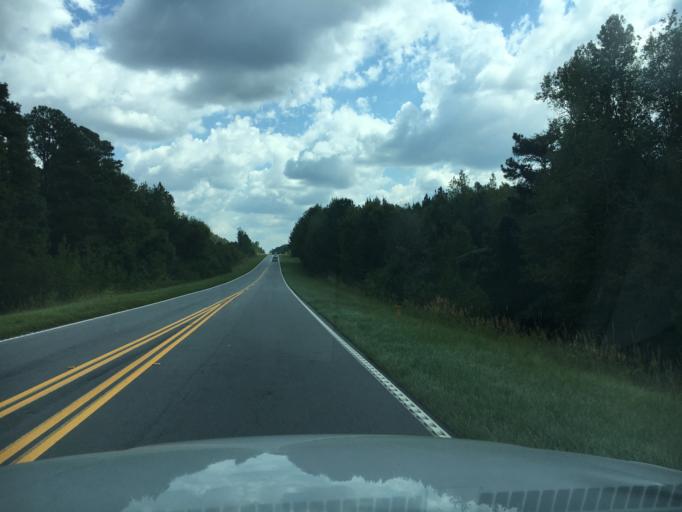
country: US
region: South Carolina
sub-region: Greenwood County
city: Greenwood
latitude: 34.1483
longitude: -82.1562
